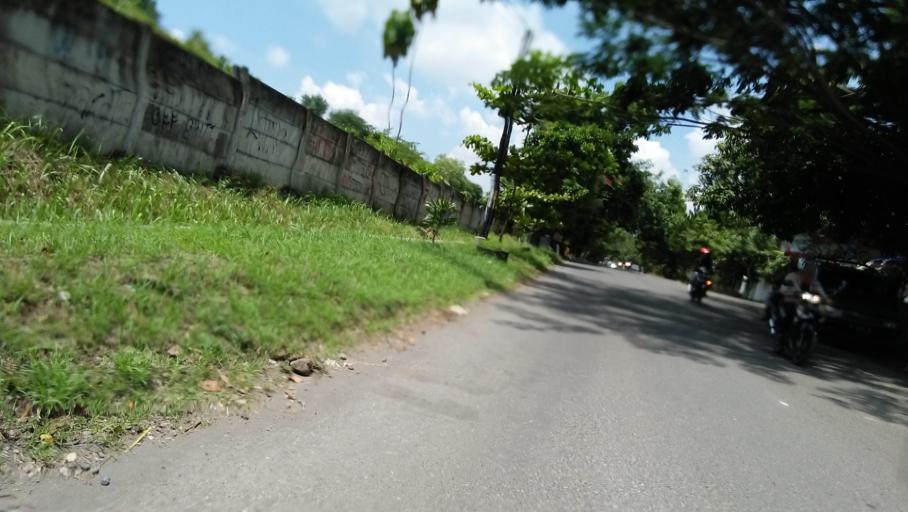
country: ID
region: Central Java
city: Mranggen
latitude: -7.0368
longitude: 110.4633
